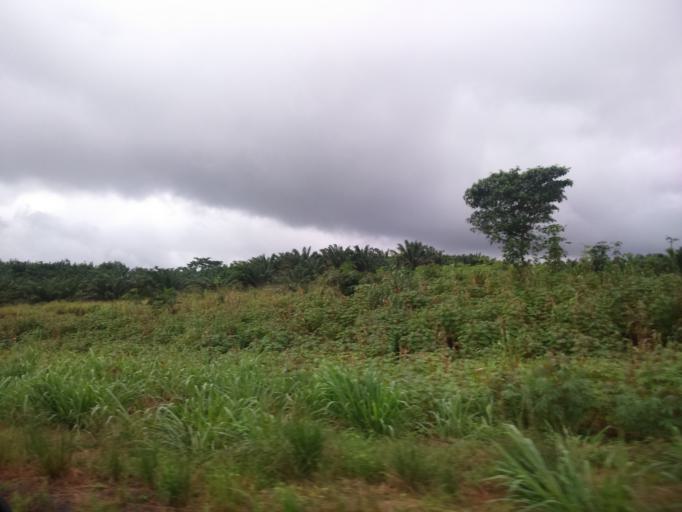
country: CI
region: Sud-Comoe
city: Adiake
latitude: 5.2995
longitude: -3.3434
